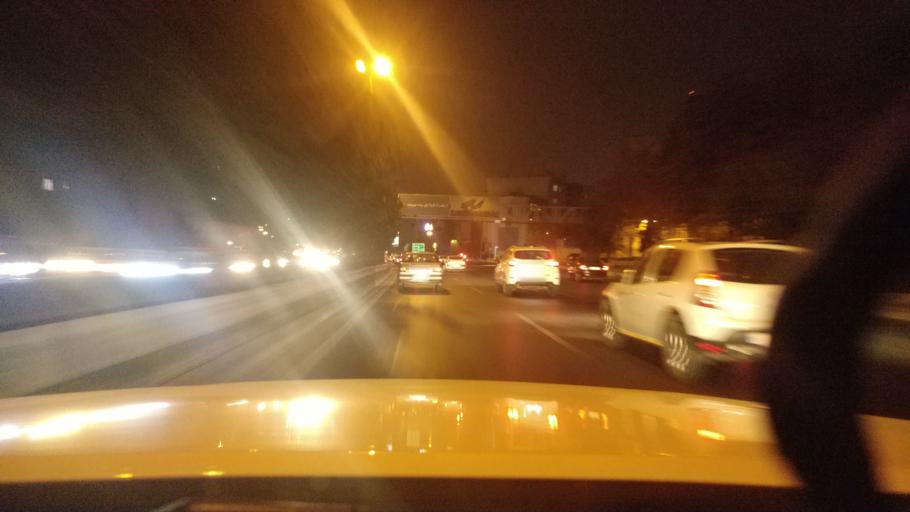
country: IR
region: Tehran
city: Tehran
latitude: 35.7365
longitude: 51.3164
